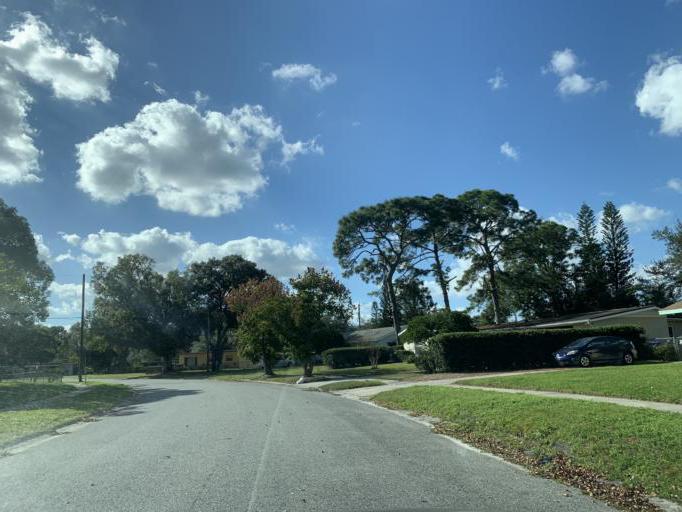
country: US
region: Florida
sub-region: Orange County
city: Eatonville
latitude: 28.6114
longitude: -81.4016
